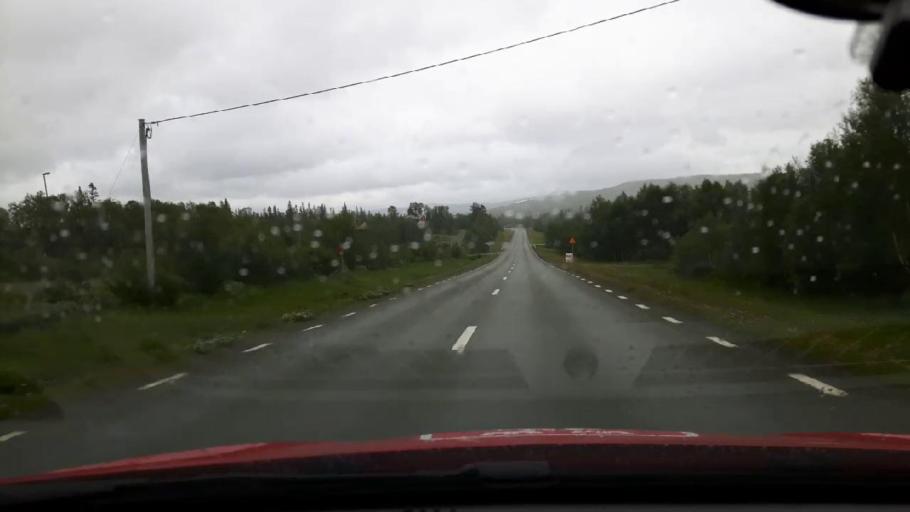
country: NO
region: Nord-Trondelag
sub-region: Meraker
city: Meraker
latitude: 63.2899
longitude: 12.1219
